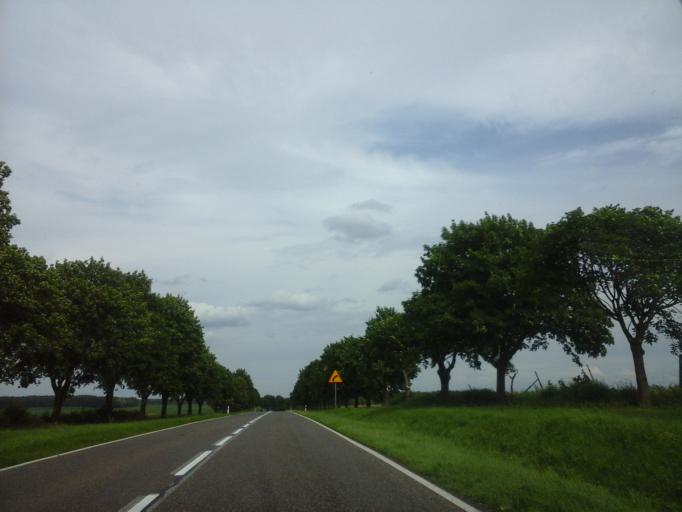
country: PL
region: West Pomeranian Voivodeship
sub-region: Powiat stargardzki
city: Suchan
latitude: 53.2754
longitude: 15.3807
